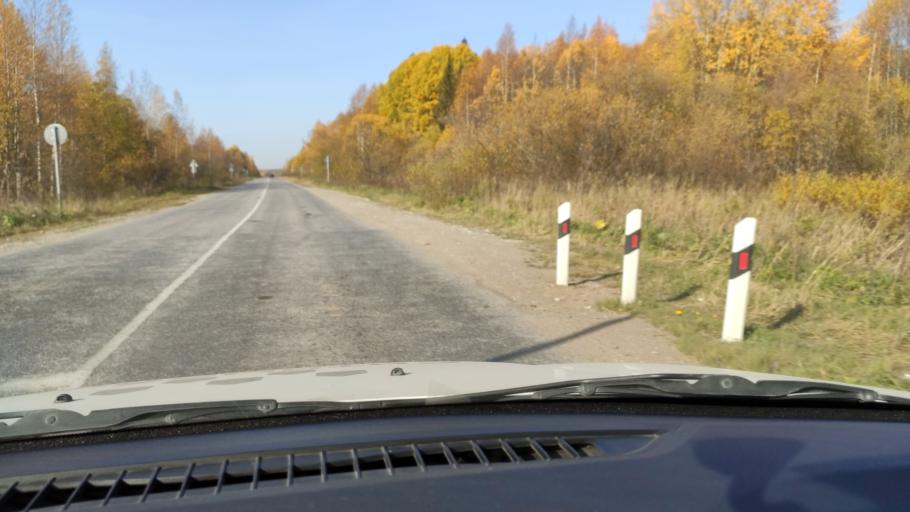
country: RU
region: Perm
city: Novyye Lyady
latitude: 58.0291
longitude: 56.6231
